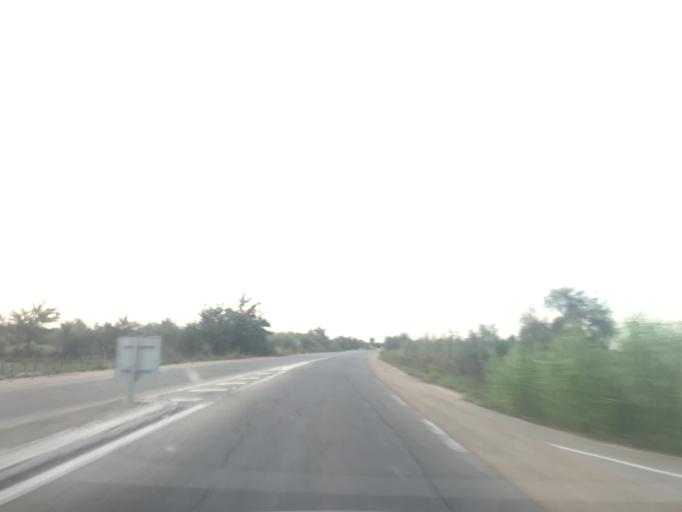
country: FR
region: Provence-Alpes-Cote d'Azur
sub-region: Departement des Bouches-du-Rhone
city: Saintes-Maries-de-la-Mer
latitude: 43.4821
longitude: 4.4048
